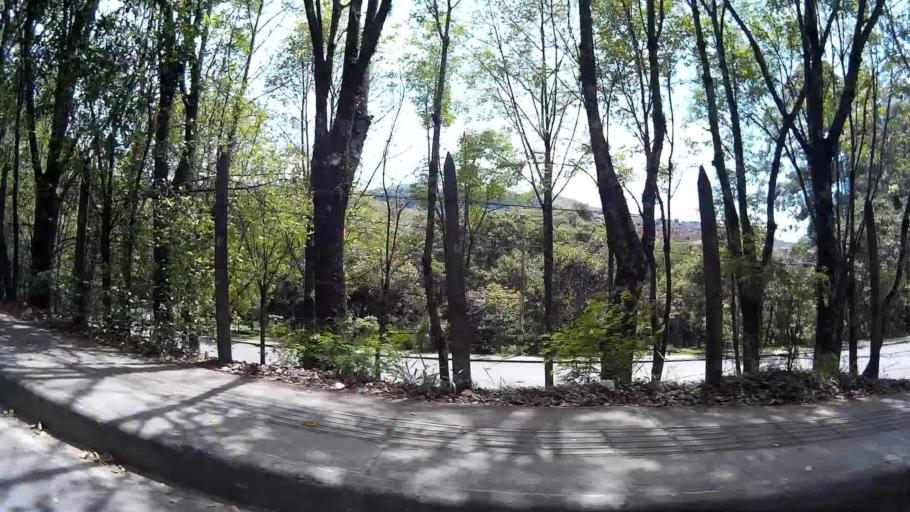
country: CO
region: Antioquia
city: Medellin
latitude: 6.2557
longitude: -75.6242
